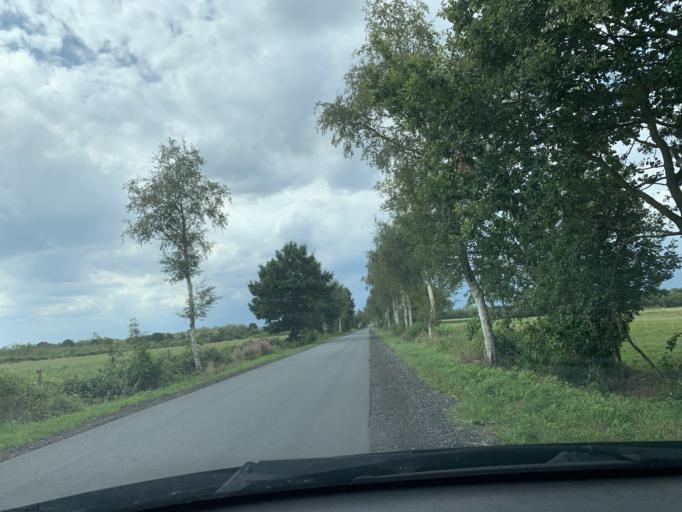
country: DE
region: Lower Saxony
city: Apen
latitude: 53.2732
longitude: 7.8246
